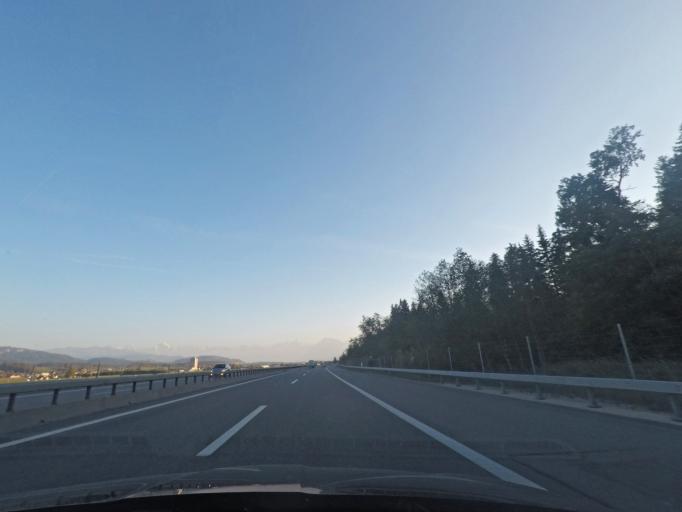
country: CH
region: Bern
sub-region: Bern-Mittelland District
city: Munsingen
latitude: 46.8550
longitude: 7.5568
